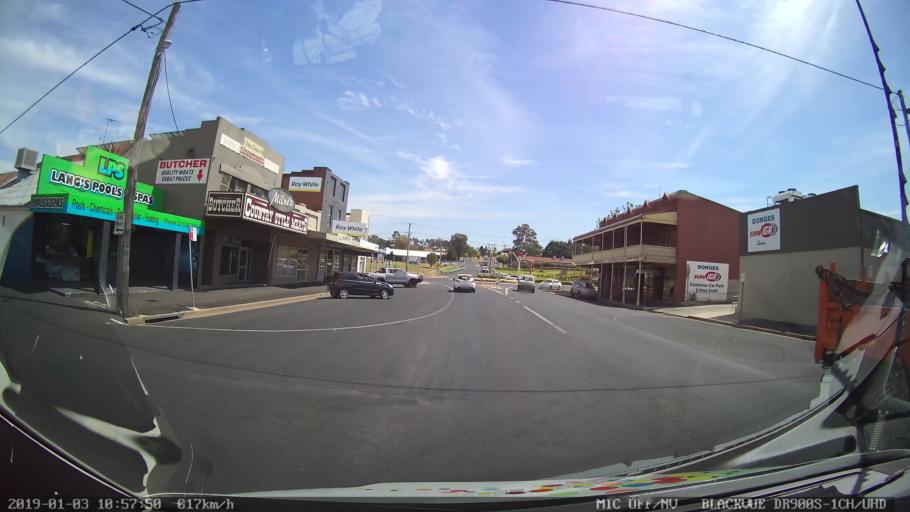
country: AU
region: New South Wales
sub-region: Young
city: Young
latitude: -34.3124
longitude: 148.2956
